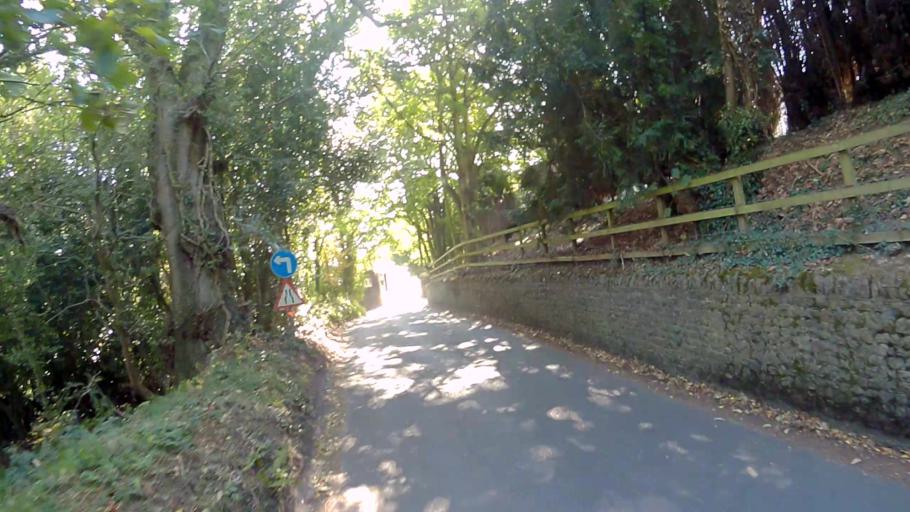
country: GB
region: England
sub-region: Surrey
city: Churt
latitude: 51.1752
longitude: -0.7864
